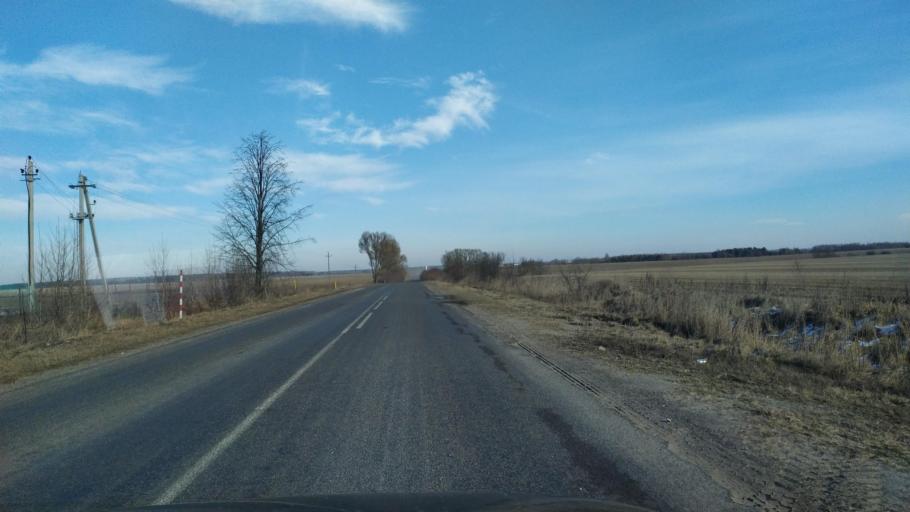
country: BY
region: Brest
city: Kamyanyets
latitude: 52.4200
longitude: 23.8063
